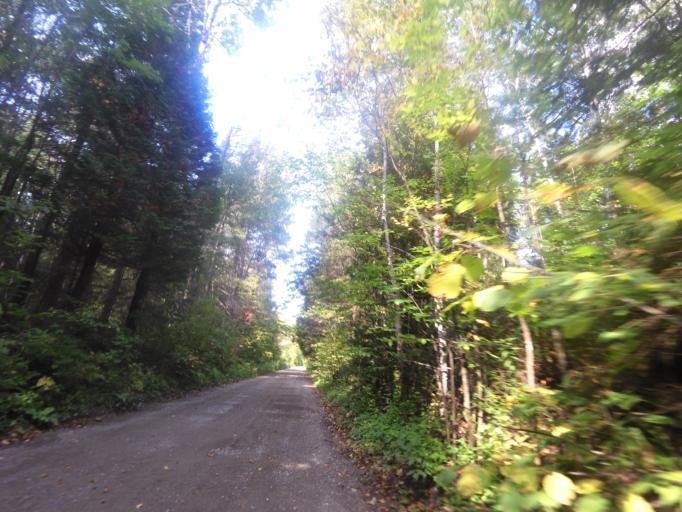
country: CA
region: Ontario
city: Renfrew
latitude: 45.1525
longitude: -76.6879
